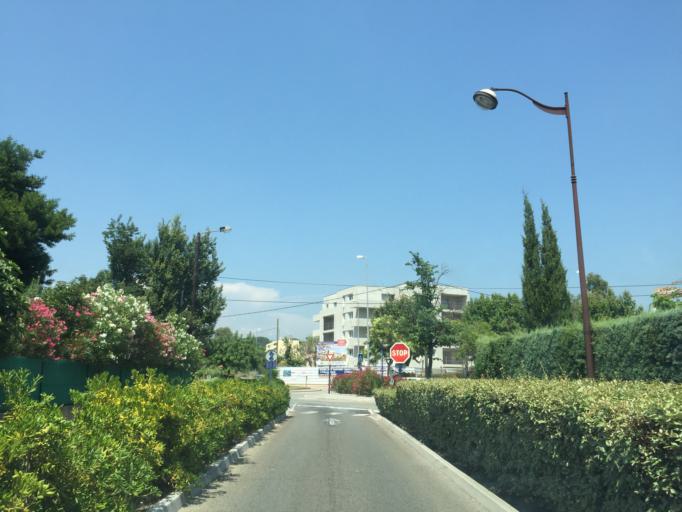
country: FR
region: Provence-Alpes-Cote d'Azur
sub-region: Departement du Var
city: Frejus
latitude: 43.4339
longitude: 6.7497
